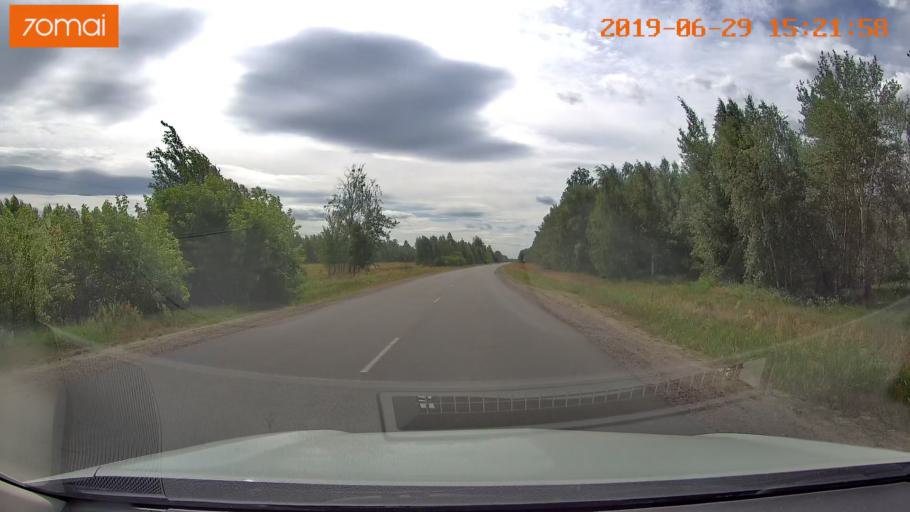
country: BY
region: Brest
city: Mikashevichy
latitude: 52.2133
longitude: 27.4531
